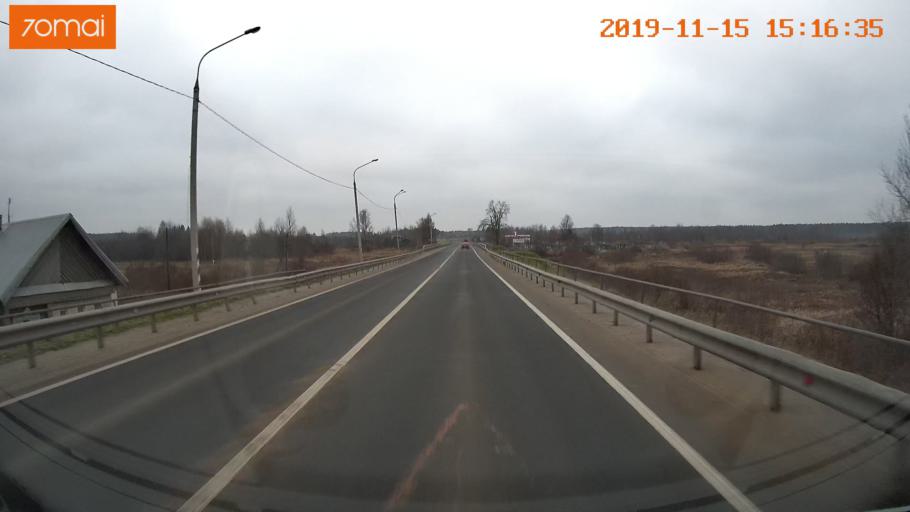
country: RU
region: Jaroslavl
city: Danilov
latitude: 58.2716
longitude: 40.1898
